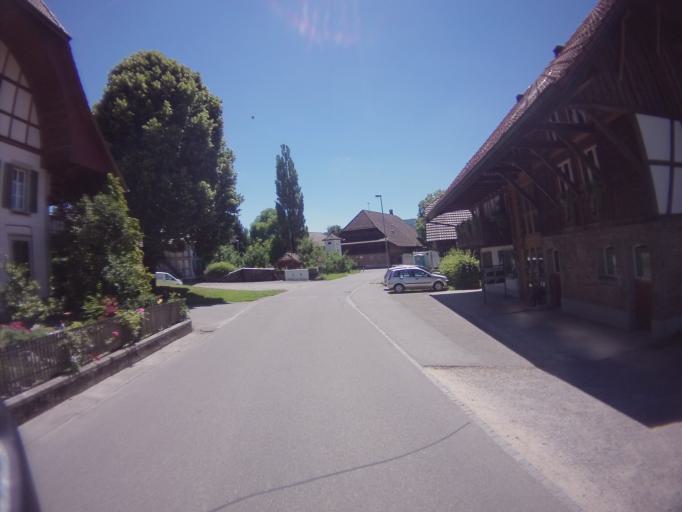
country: CH
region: Bern
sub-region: Bern-Mittelland District
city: Urtenen
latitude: 47.0308
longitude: 7.5135
